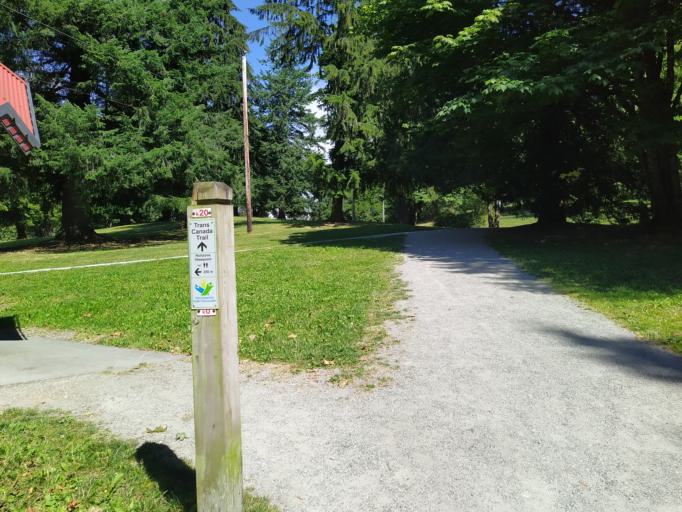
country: CA
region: British Columbia
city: Burnaby
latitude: 49.2805
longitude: -122.9350
